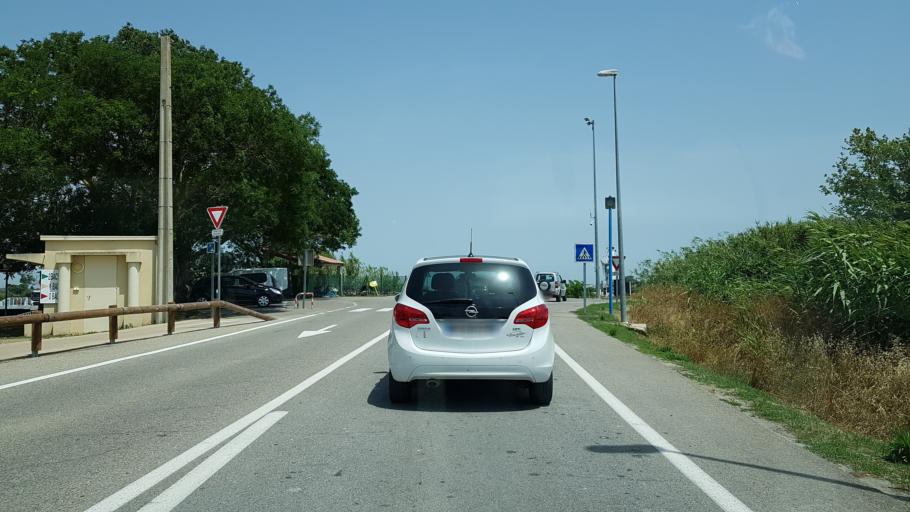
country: FR
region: Provence-Alpes-Cote d'Azur
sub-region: Departement des Bouches-du-Rhone
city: Port-Saint-Louis-du-Rhone
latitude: 43.4181
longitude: 4.7422
